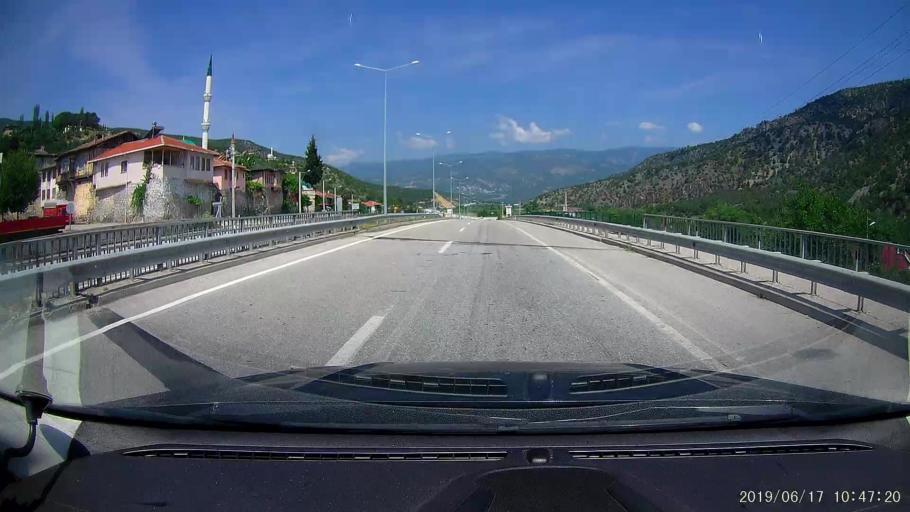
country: TR
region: Corum
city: Hacihamza
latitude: 41.0763
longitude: 34.4504
